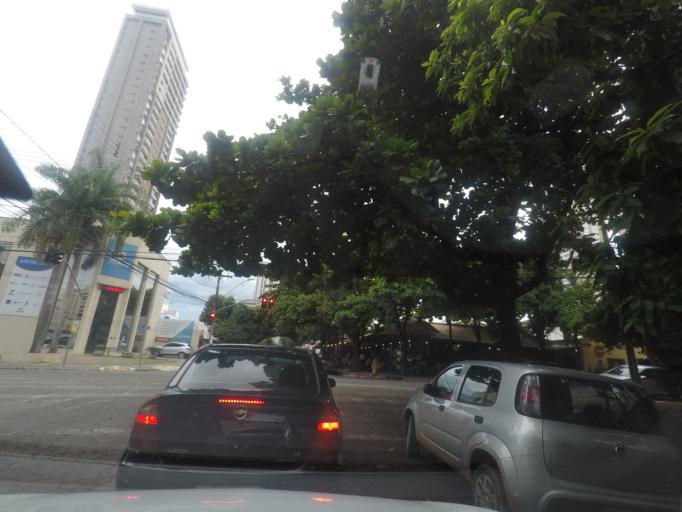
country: BR
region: Goias
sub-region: Goiania
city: Goiania
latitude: -16.6906
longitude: -49.2692
